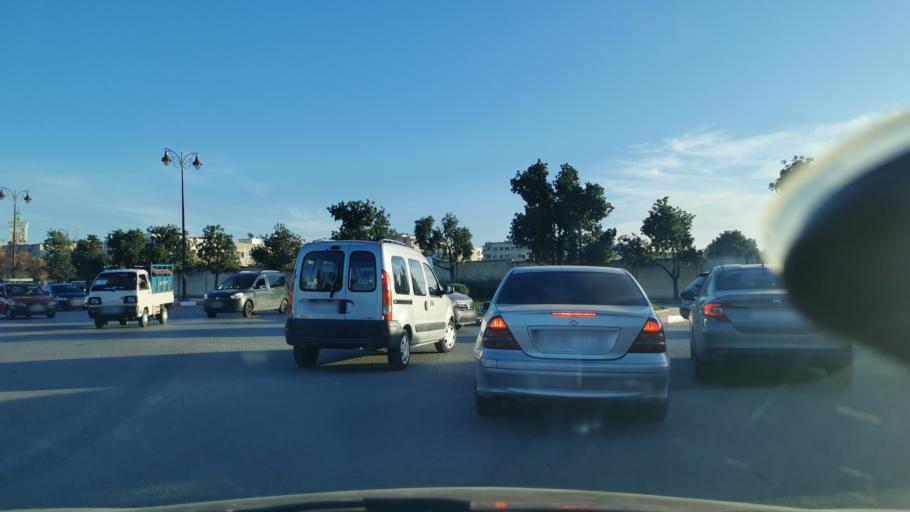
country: MA
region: Fes-Boulemane
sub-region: Fes
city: Fes
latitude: 34.0213
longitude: -4.9824
